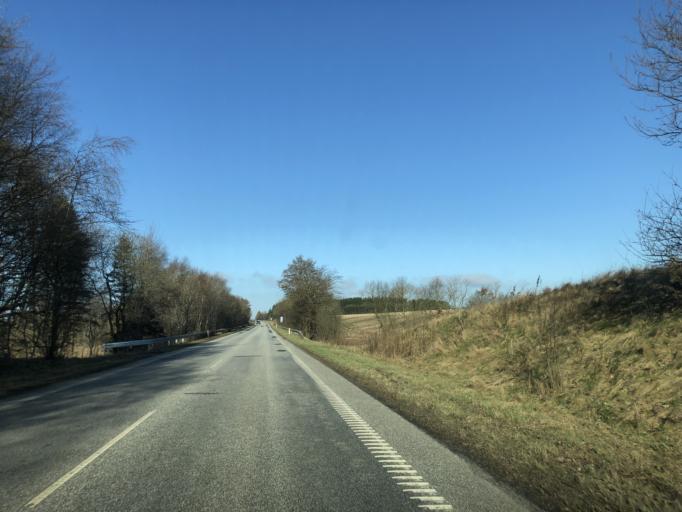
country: DK
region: North Denmark
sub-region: Vesthimmerland Kommune
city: Alestrup
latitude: 56.6173
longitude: 9.6067
